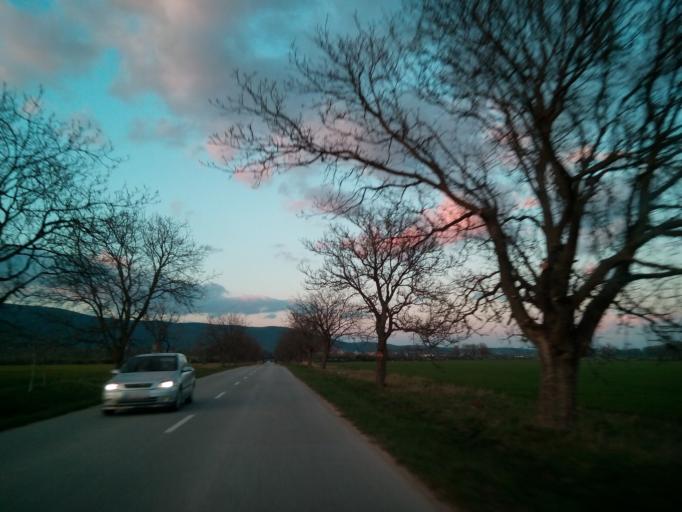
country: SK
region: Kosicky
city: Medzev
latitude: 48.5901
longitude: 20.8583
